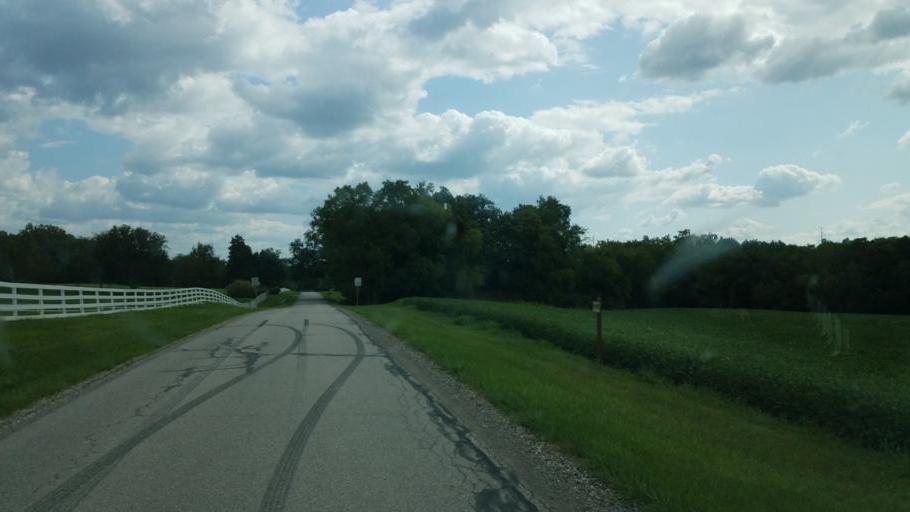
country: US
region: Ohio
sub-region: Delaware County
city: Lewis Center
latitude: 40.2235
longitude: -83.0612
